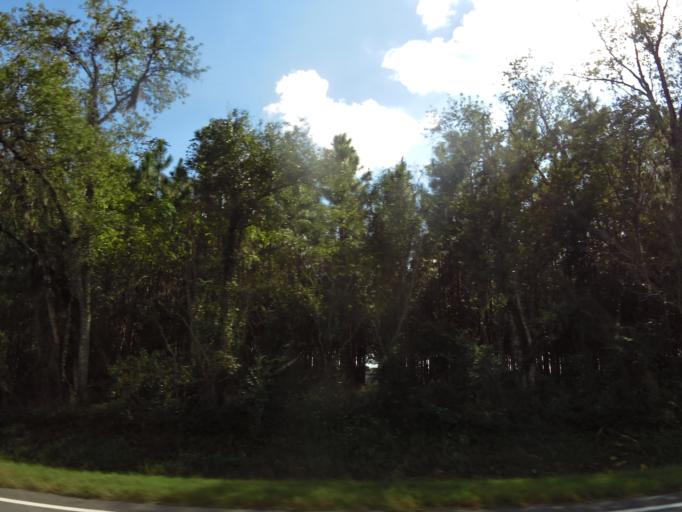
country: US
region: Georgia
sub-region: Lowndes County
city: Valdosta
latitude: 30.8099
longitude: -83.2257
